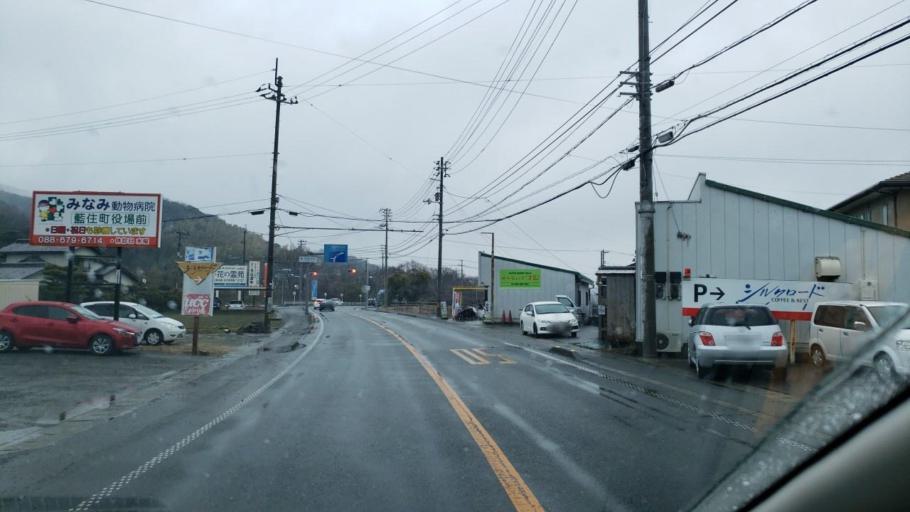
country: JP
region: Tokushima
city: Tokushima-shi
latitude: 34.1587
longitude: 134.5066
